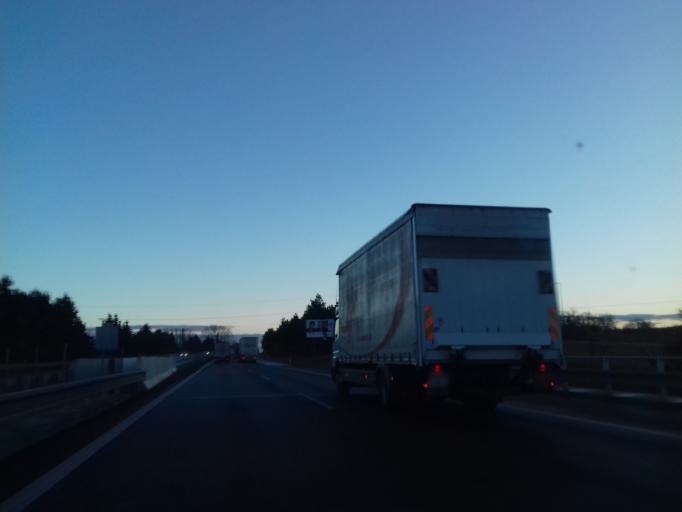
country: CZ
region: South Moravian
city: Rousinov
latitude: 49.1944
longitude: 16.8884
